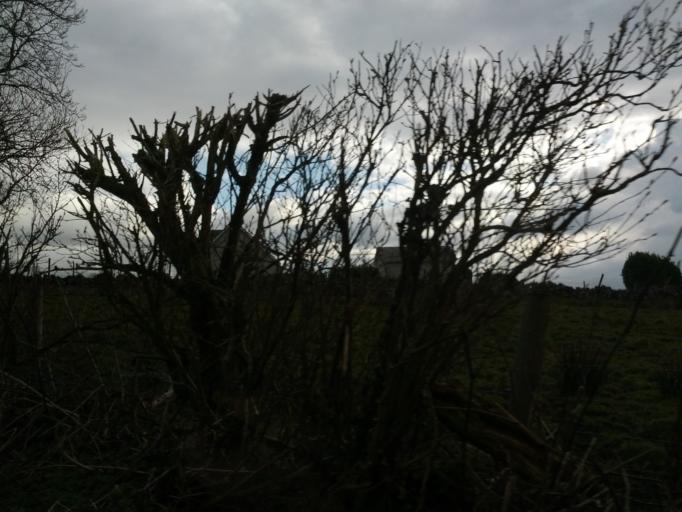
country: IE
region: Connaught
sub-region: County Galway
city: Athenry
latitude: 53.4238
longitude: -8.6163
